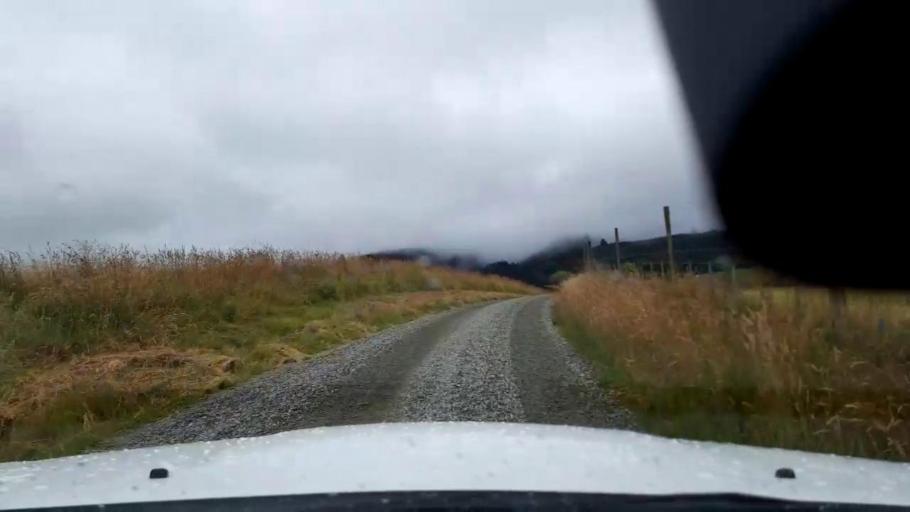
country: NZ
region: Canterbury
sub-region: Timaru District
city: Pleasant Point
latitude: -44.0753
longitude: 171.1466
